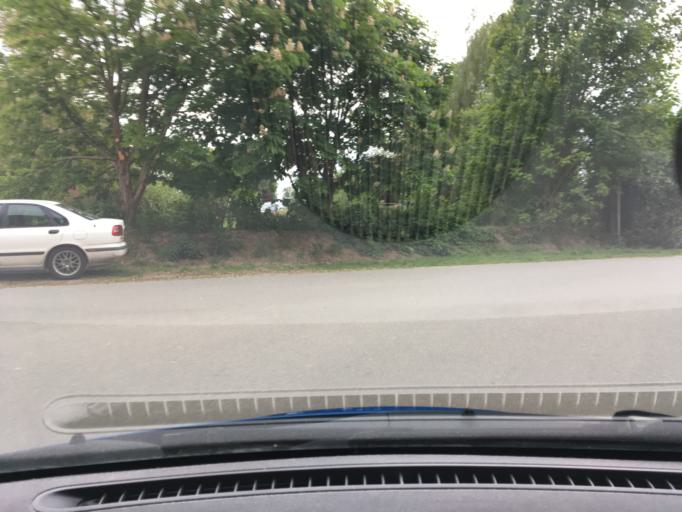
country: DE
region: Lower Saxony
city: Eyendorf
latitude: 53.1990
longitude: 10.1503
